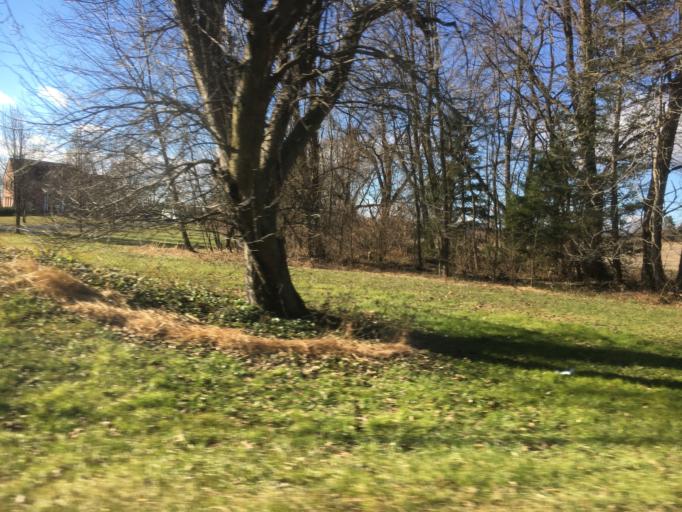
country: US
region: Pennsylvania
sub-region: Lehigh County
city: Egypt
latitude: 40.6446
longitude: -75.5474
